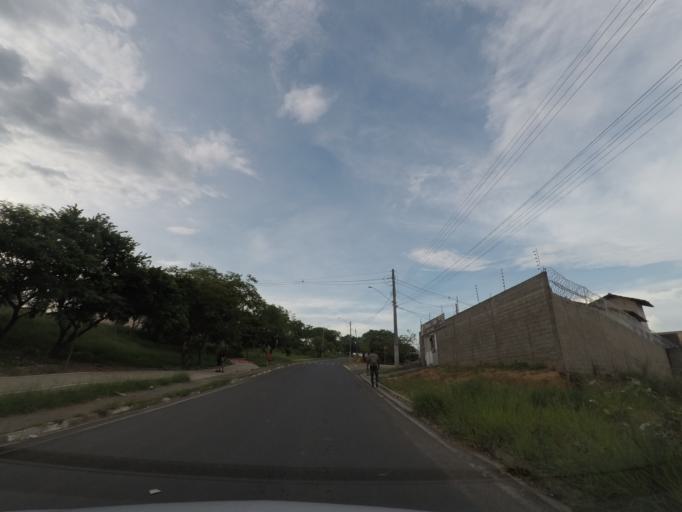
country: BR
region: Sao Paulo
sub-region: Hortolandia
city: Hortolandia
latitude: -22.9594
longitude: -47.1897
